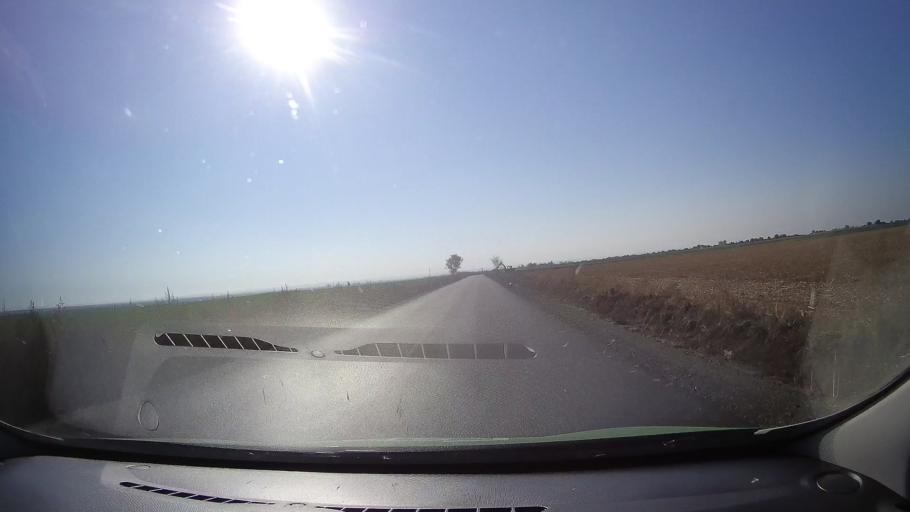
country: RO
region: Satu Mare
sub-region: Comuna Tiream
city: Tiream
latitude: 47.6359
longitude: 22.4666
